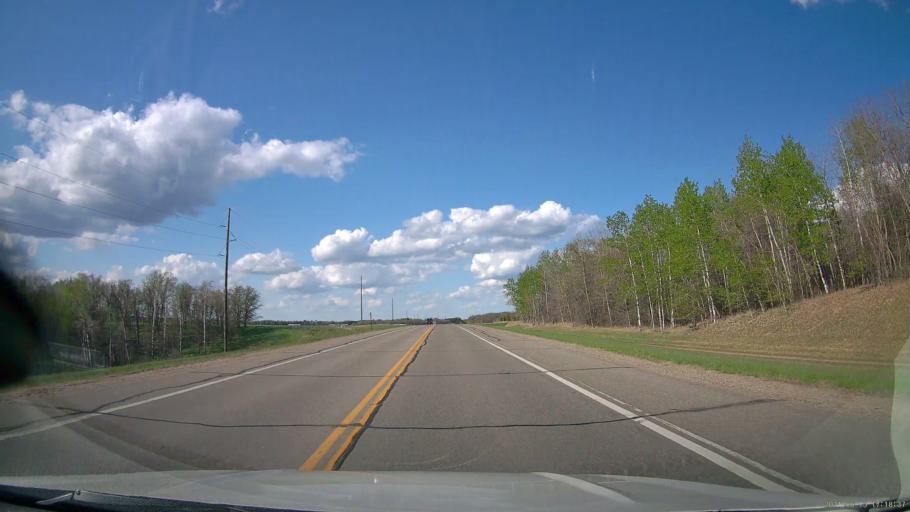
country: US
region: Minnesota
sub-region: Hubbard County
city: Park Rapids
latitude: 46.9644
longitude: -95.0175
